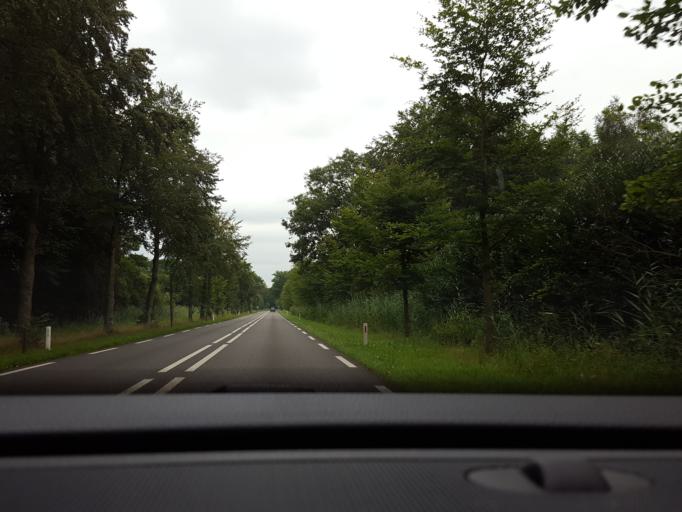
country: NL
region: Gelderland
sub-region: Gemeente Rheden
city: Spankeren
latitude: 52.0888
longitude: 6.1228
